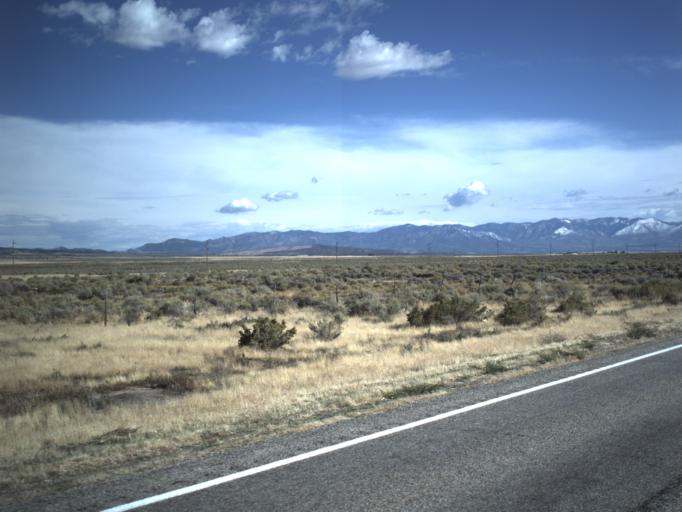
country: US
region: Utah
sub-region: Millard County
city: Delta
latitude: 39.2560
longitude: -112.4429
